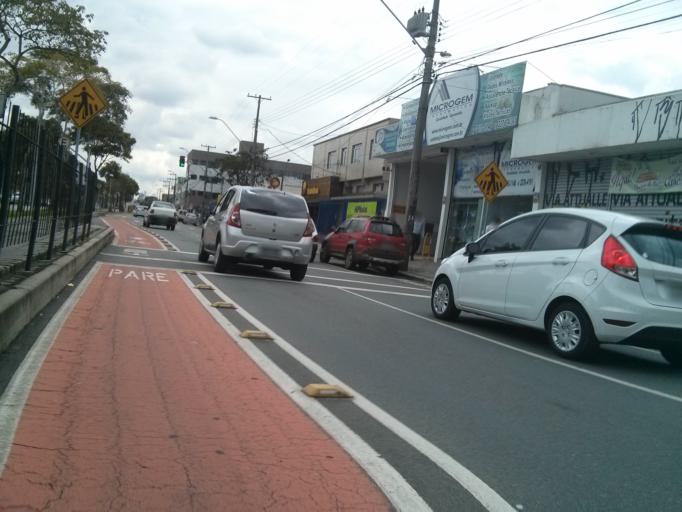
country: BR
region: Parana
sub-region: Curitiba
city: Curitiba
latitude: -25.4759
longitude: -49.2499
